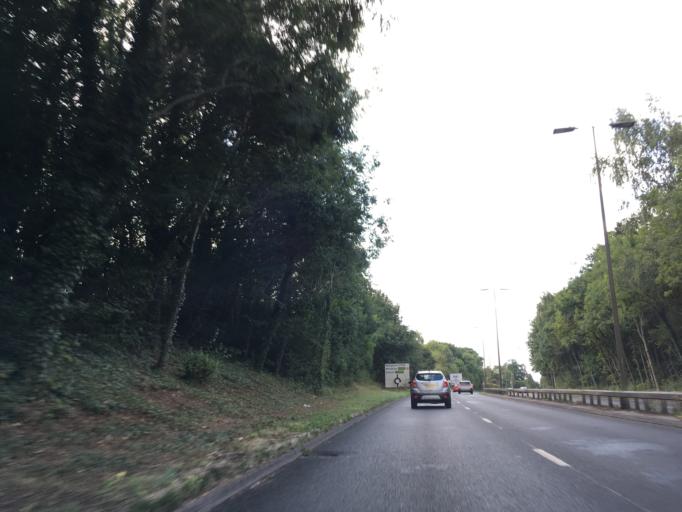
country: GB
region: England
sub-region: West Berkshire
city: Greenham
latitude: 51.3872
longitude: -1.3200
